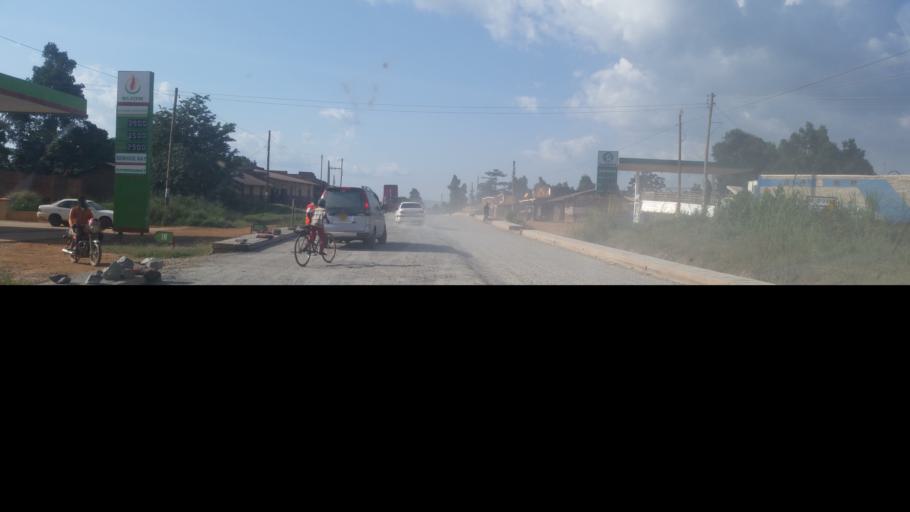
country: UG
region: Western Region
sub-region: Hoima District
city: Hoima
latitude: 1.4028
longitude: 31.3337
